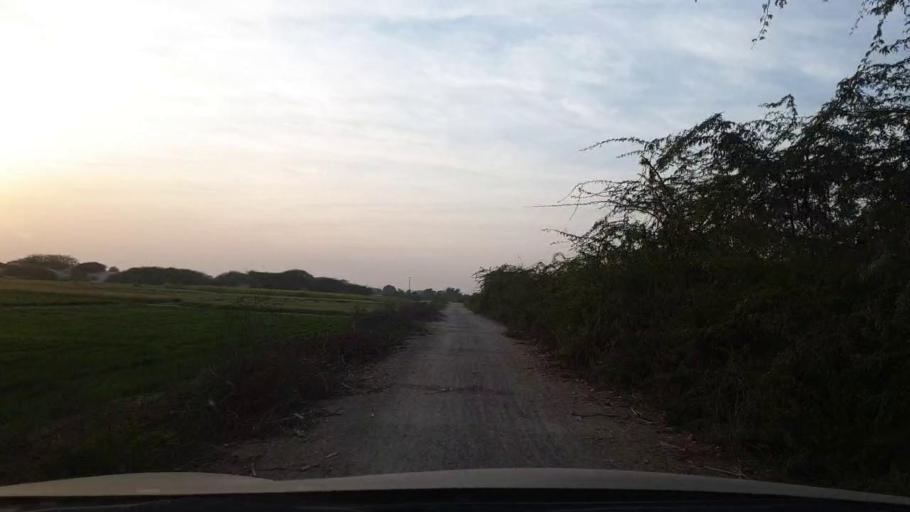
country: PK
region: Sindh
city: Tando Adam
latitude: 25.6764
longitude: 68.7099
